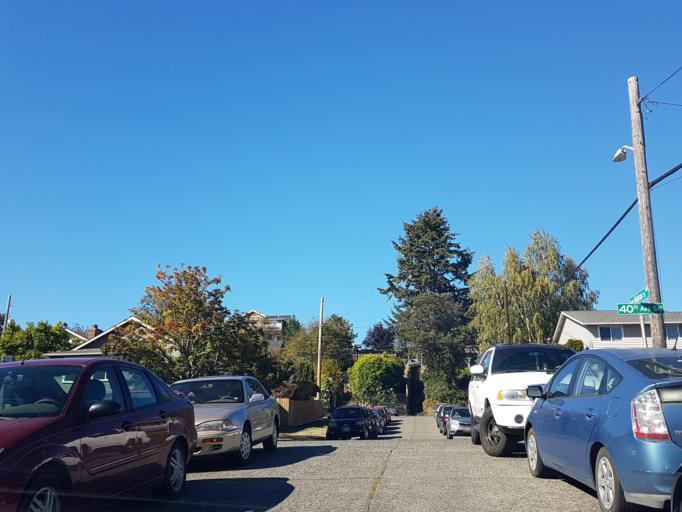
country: US
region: Washington
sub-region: King County
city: White Center
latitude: 47.5575
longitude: -122.3825
